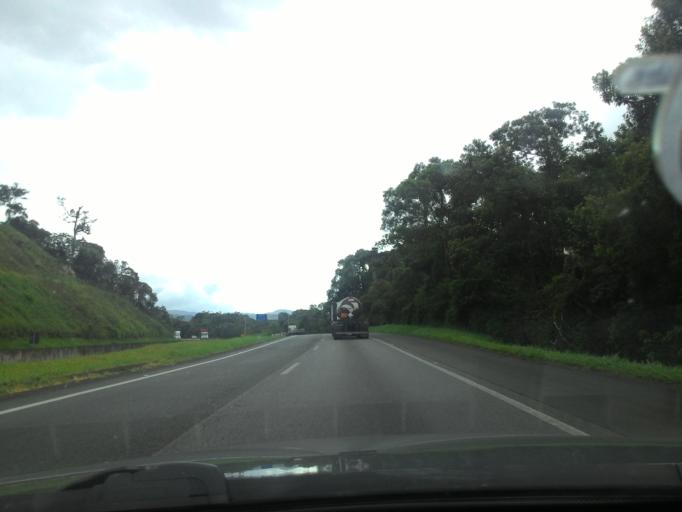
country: BR
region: Sao Paulo
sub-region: Cajati
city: Cajati
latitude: -24.9685
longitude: -48.3941
